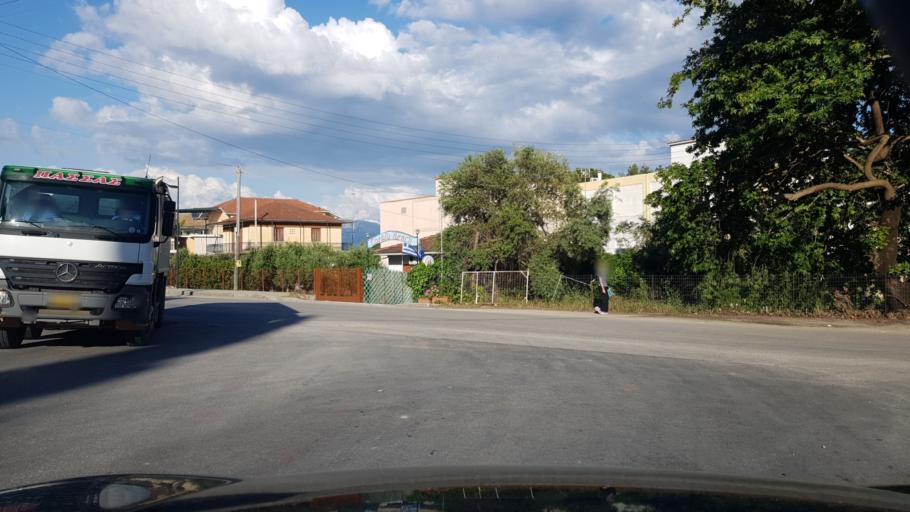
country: GR
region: Ionian Islands
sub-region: Lefkada
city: Nidri
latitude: 38.7169
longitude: 20.7169
